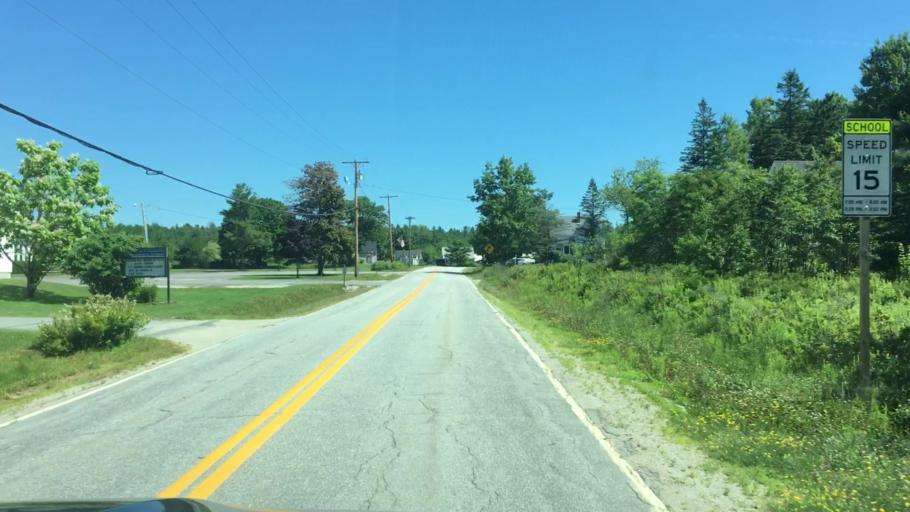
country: US
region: Maine
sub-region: Hancock County
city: Penobscot
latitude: 44.4677
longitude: -68.7091
